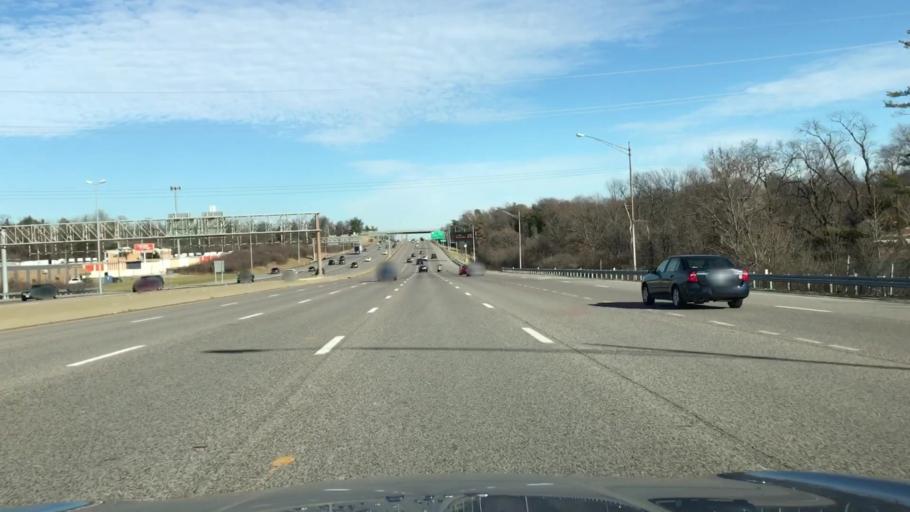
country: US
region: Missouri
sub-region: Saint Louis County
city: Bridgeton
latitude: 38.7585
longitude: -90.4306
